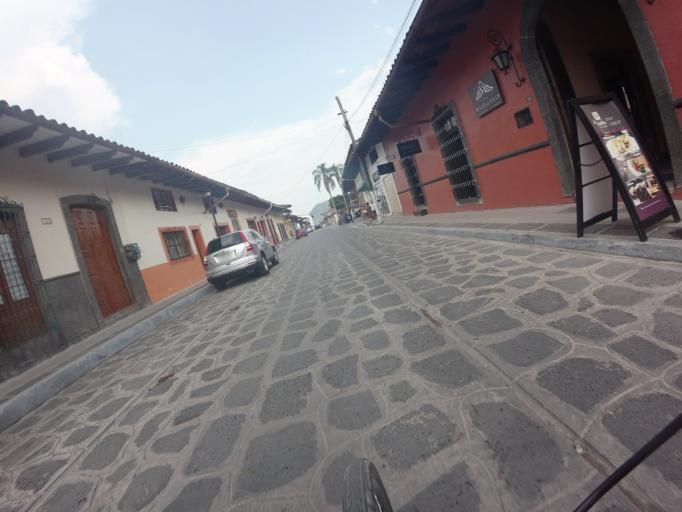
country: MX
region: Veracruz
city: Xico
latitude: 19.4211
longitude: -97.0065
